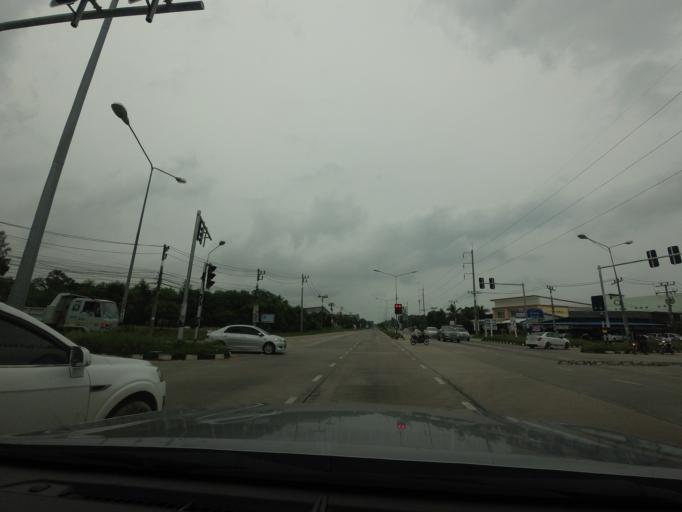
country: TH
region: Songkhla
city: Singhanakhon
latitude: 7.3476
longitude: 100.4796
